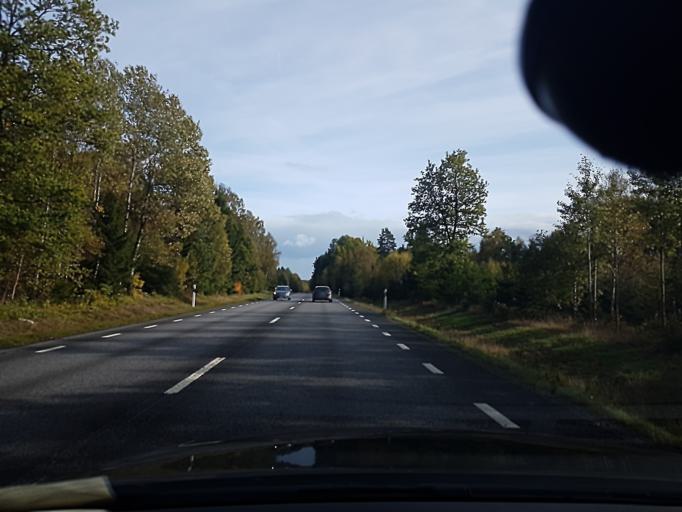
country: SE
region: Joenkoeping
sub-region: Varnamo Kommun
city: Bor
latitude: 57.1418
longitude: 14.1050
